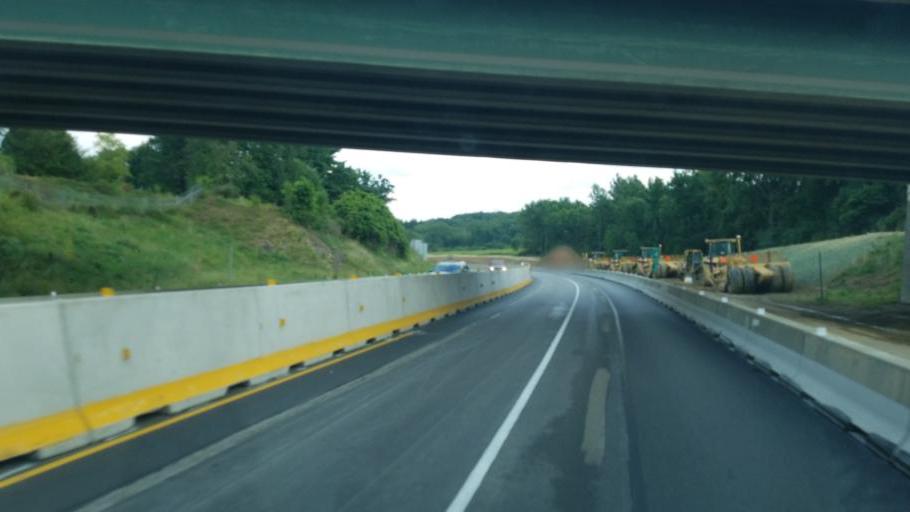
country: US
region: Pennsylvania
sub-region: Allegheny County
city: Gibsonia
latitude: 40.5999
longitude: -79.9308
